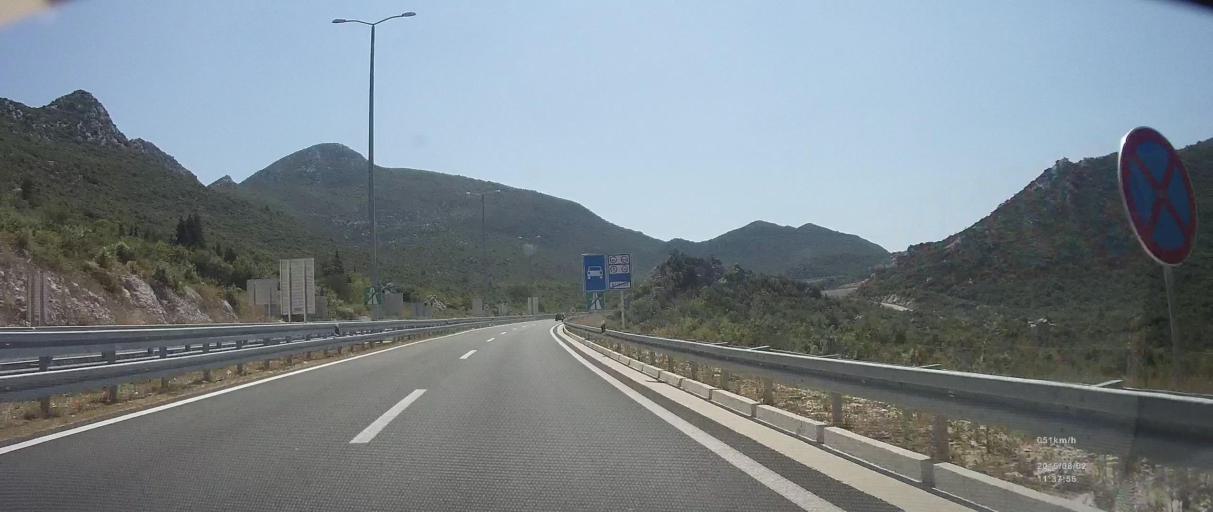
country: HR
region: Dubrovacko-Neretvanska
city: Komin
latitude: 43.1004
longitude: 17.4873
